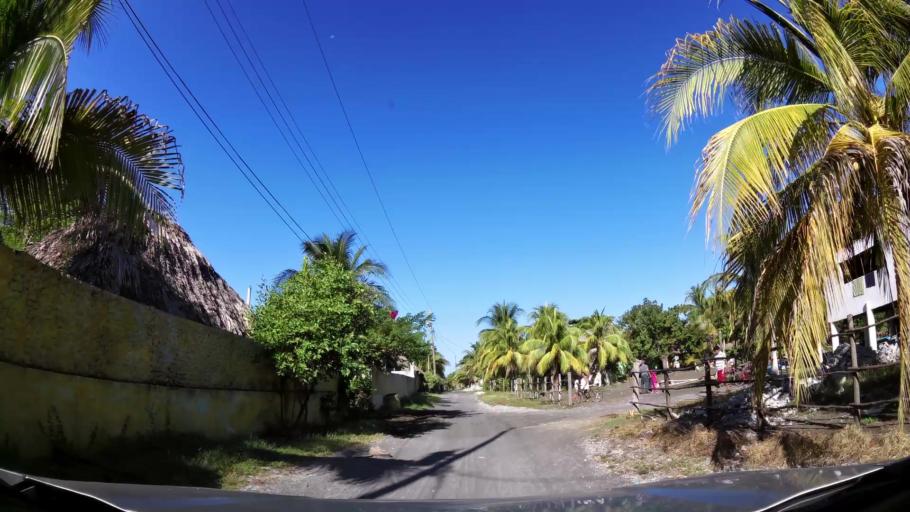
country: GT
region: Santa Rosa
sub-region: Municipio de Taxisco
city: Taxisco
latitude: 13.8915
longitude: -90.4873
